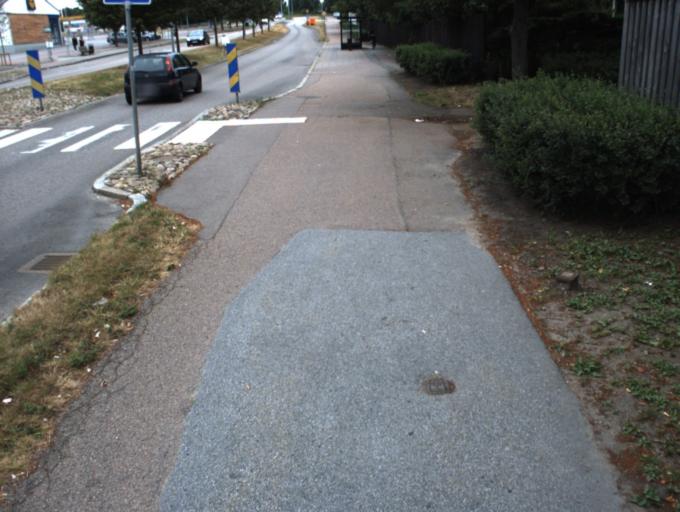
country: SE
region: Skane
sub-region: Helsingborg
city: Odakra
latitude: 56.0666
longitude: 12.7256
